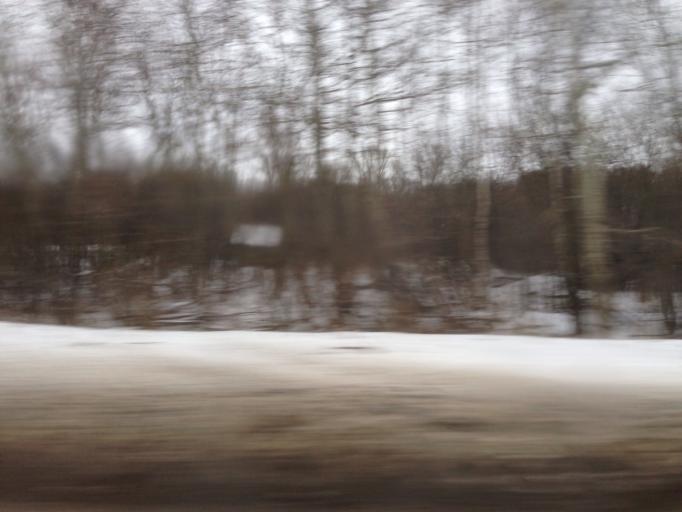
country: RU
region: Tula
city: Uzlovaya
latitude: 54.0048
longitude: 38.1746
